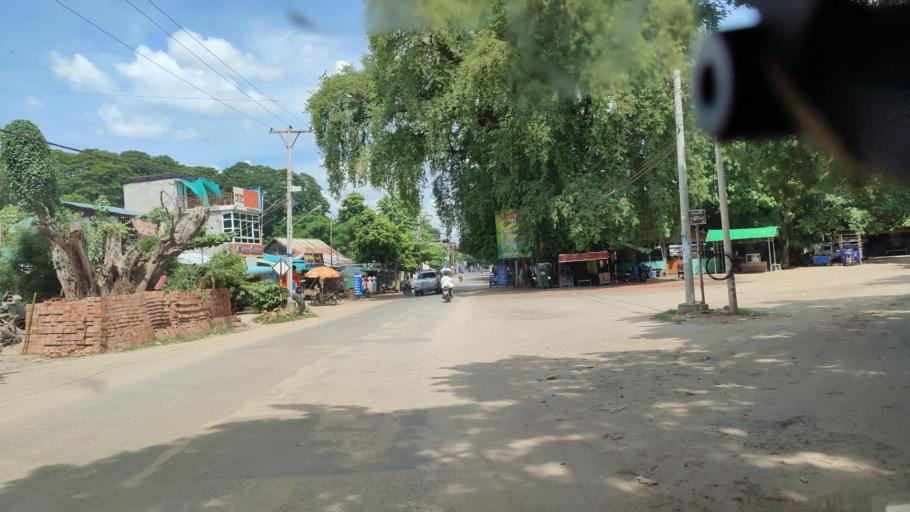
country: MM
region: Magway
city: Pakokku
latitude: 21.1976
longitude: 94.9037
